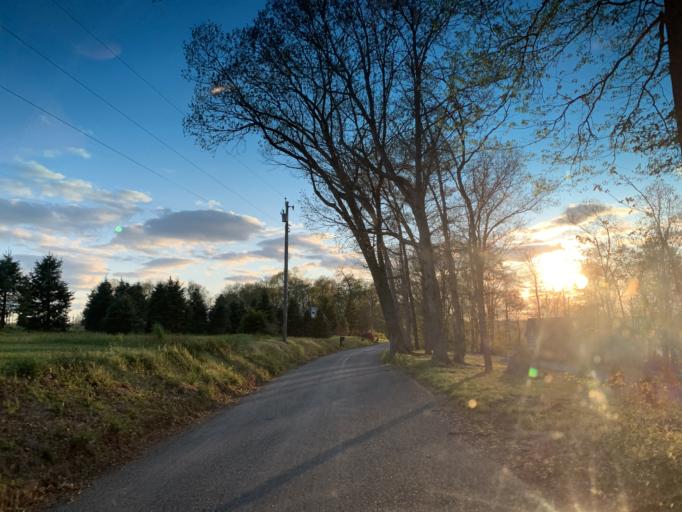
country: US
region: Maryland
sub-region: Harford County
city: Jarrettsville
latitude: 39.6560
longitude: -76.4282
